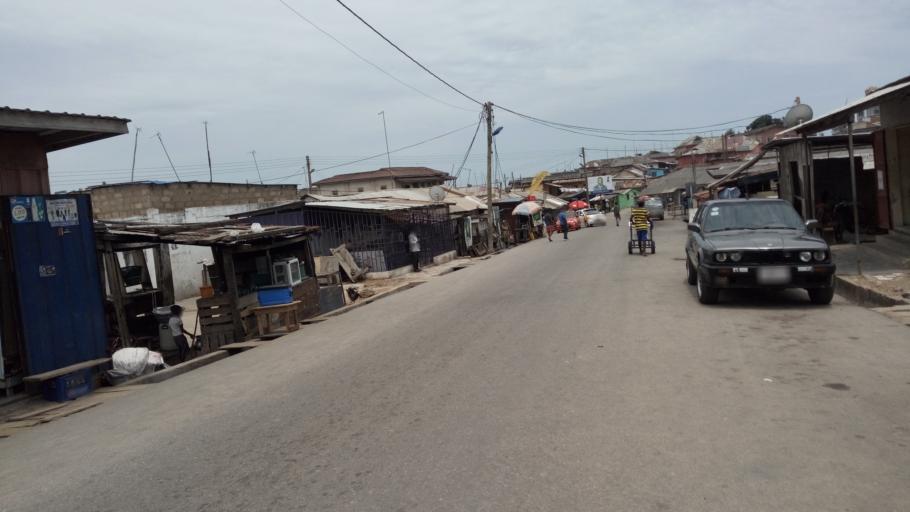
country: GH
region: Central
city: Winneba
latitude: 5.3405
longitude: -0.6219
